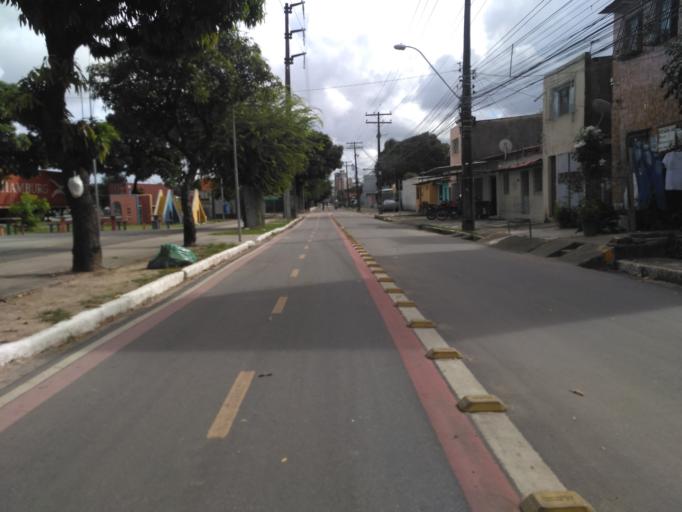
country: BR
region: Pernambuco
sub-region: Recife
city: Recife
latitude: -8.0379
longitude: -34.8761
